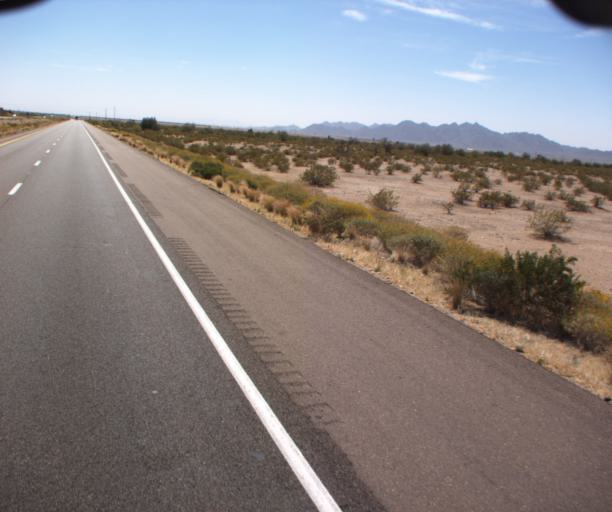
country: US
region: Arizona
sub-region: Maricopa County
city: Buckeye
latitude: 33.1792
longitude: -112.6508
